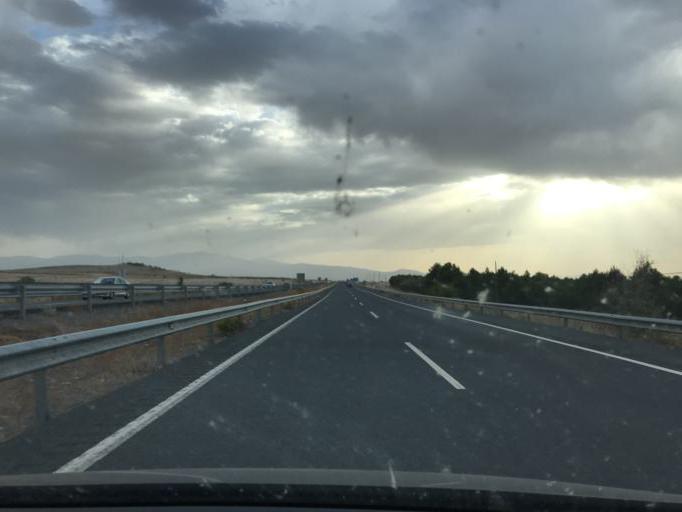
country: ES
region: Andalusia
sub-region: Provincia de Granada
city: Gor
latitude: 37.3862
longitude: -3.0488
